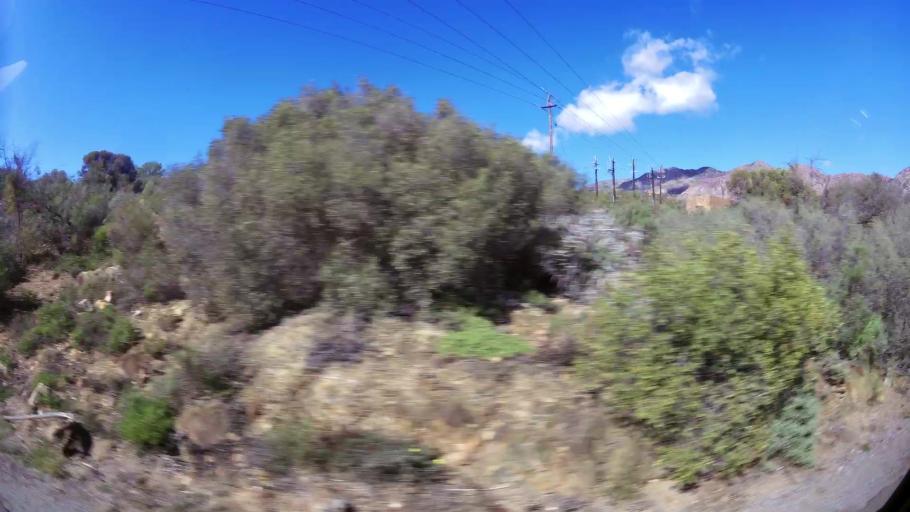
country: ZA
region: Western Cape
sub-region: Cape Winelands District Municipality
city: Ashton
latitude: -33.7900
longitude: 20.1316
